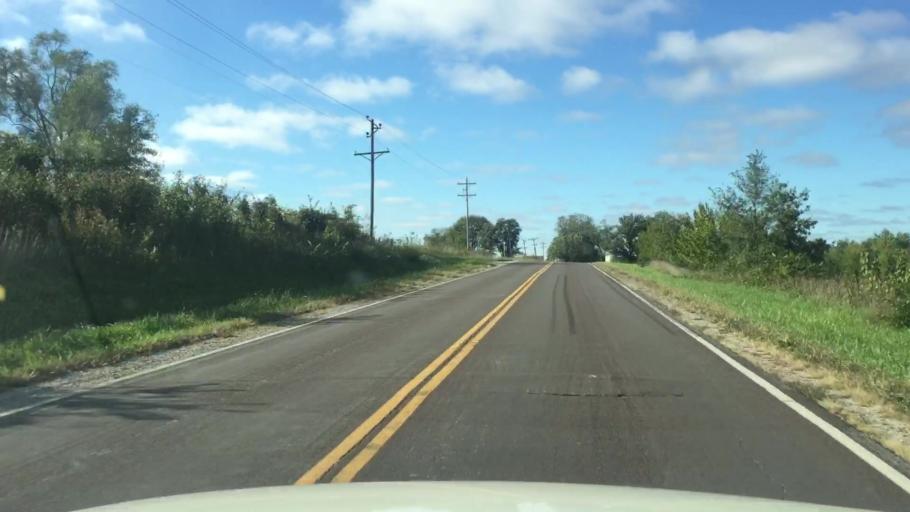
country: US
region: Missouri
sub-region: Howard County
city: Fayette
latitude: 39.1013
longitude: -92.7357
